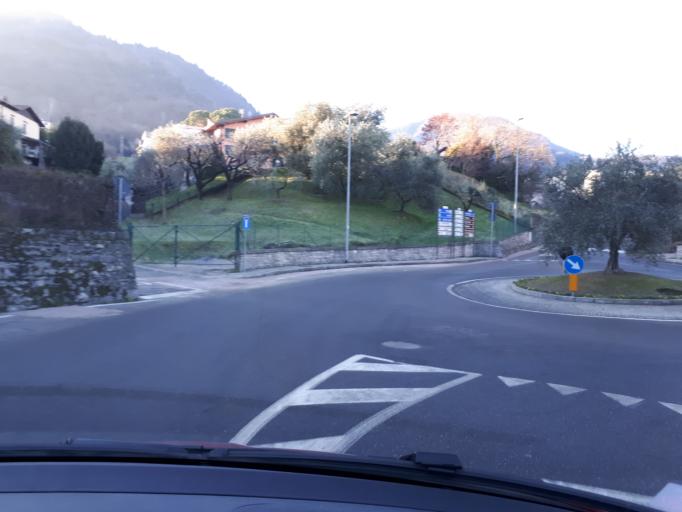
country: IT
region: Lombardy
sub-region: Provincia di Como
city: Bellagio
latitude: 45.9726
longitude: 9.2606
